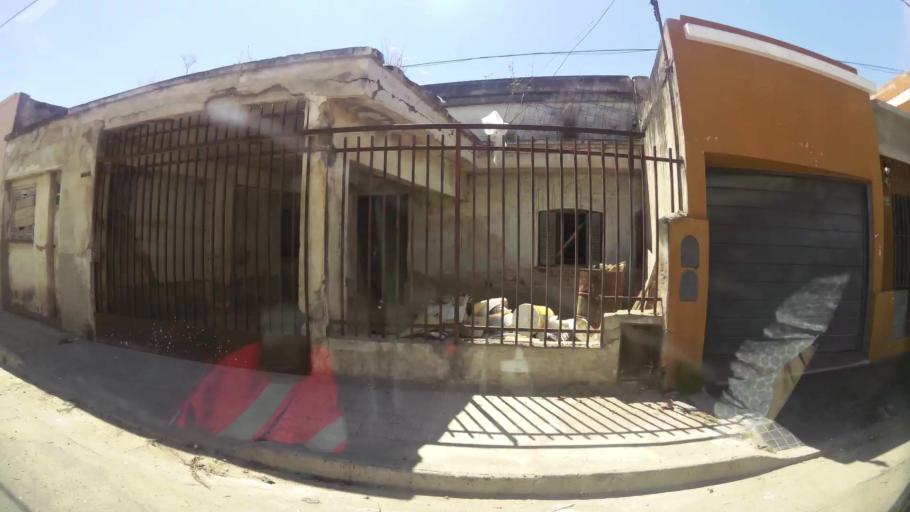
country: AR
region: Cordoba
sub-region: Departamento de Capital
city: Cordoba
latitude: -31.4282
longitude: -64.2079
